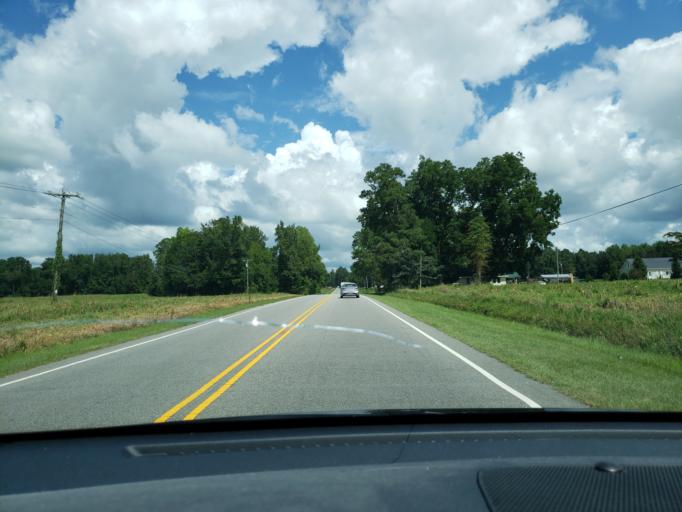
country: US
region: North Carolina
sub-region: Columbus County
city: Brunswick
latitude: 34.2624
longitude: -78.7434
